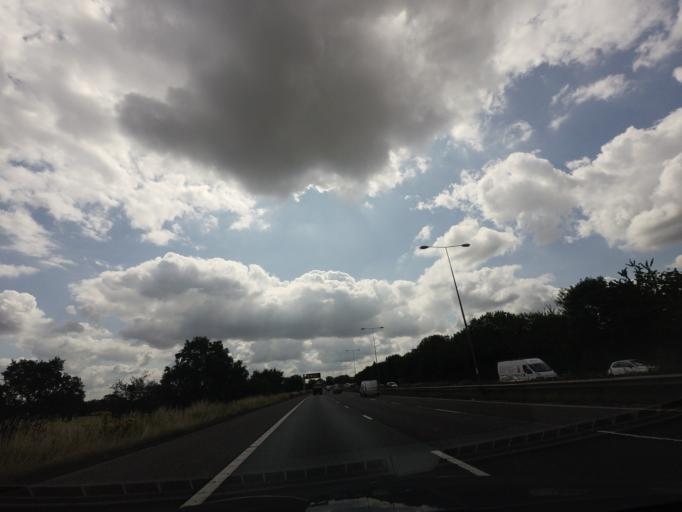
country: GB
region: England
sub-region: Borough of Wigan
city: Shevington
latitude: 53.5462
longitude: -2.6982
